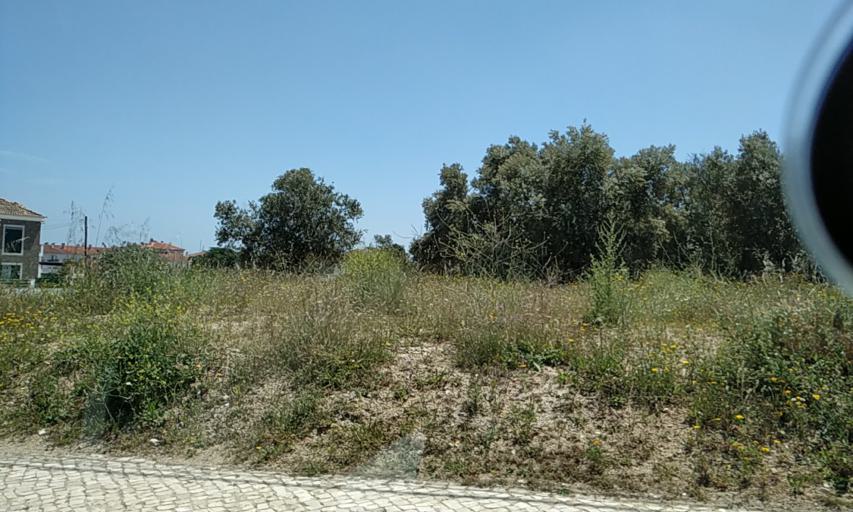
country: PT
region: Setubal
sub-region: Palmela
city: Palmela
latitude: 38.5709
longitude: -8.8855
